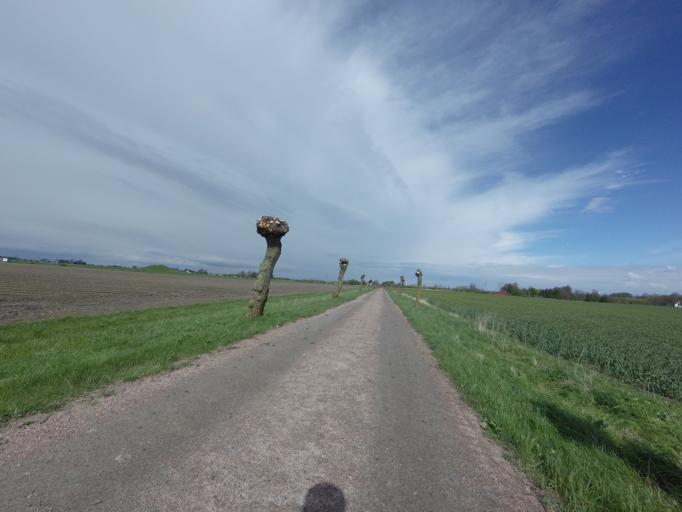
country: SE
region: Skane
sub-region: Malmo
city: Bunkeflostrand
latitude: 55.5399
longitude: 12.9724
